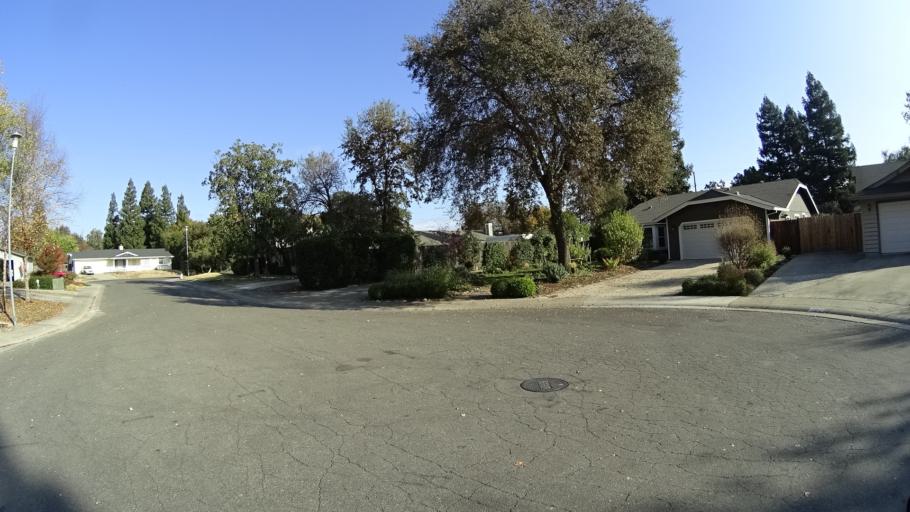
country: US
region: California
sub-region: Sacramento County
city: Citrus Heights
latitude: 38.7107
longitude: -121.2680
